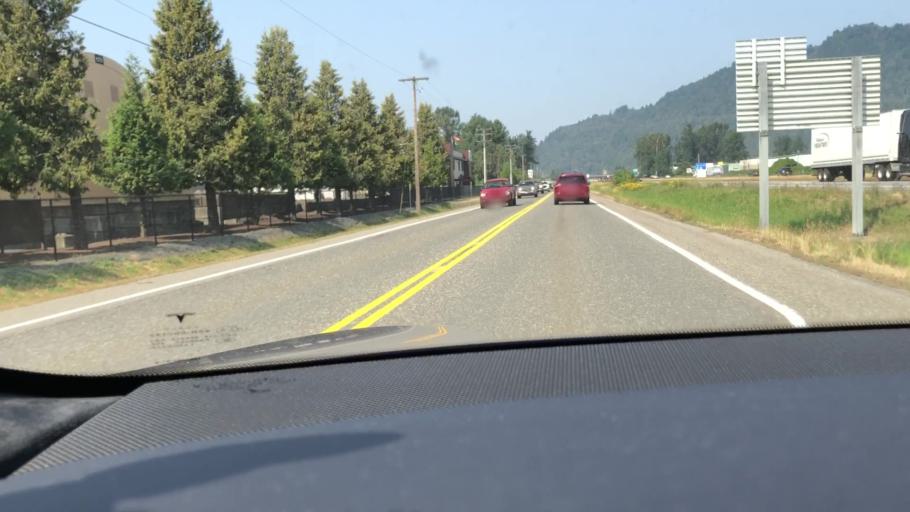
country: CA
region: British Columbia
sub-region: Fraser Valley Regional District
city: Chilliwack
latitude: 49.1431
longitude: -121.9947
